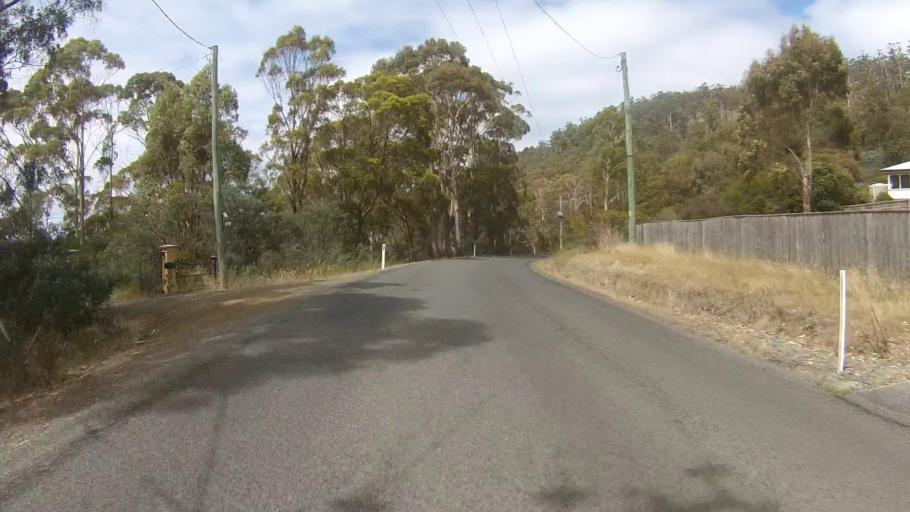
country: AU
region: Tasmania
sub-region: Kingborough
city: Blackmans Bay
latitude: -43.0232
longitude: 147.3233
